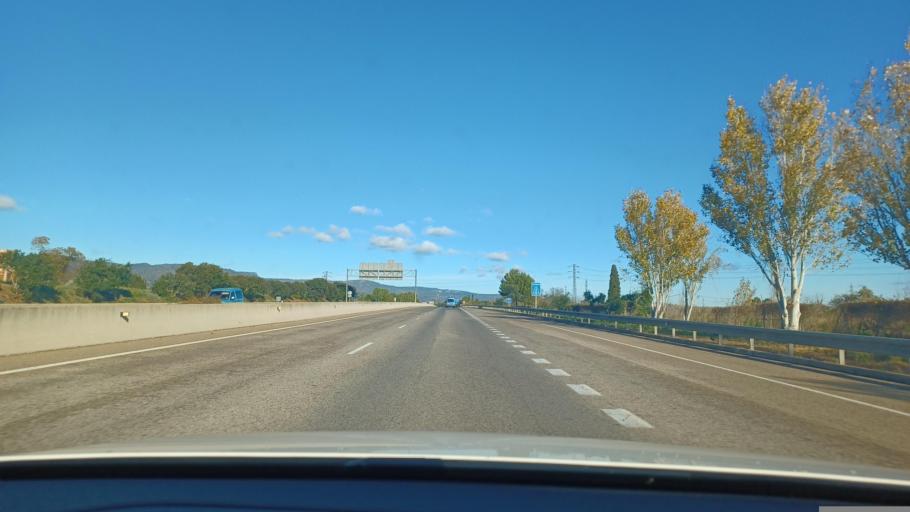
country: ES
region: Catalonia
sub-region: Provincia de Tarragona
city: Reus
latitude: 41.1568
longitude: 1.1426
